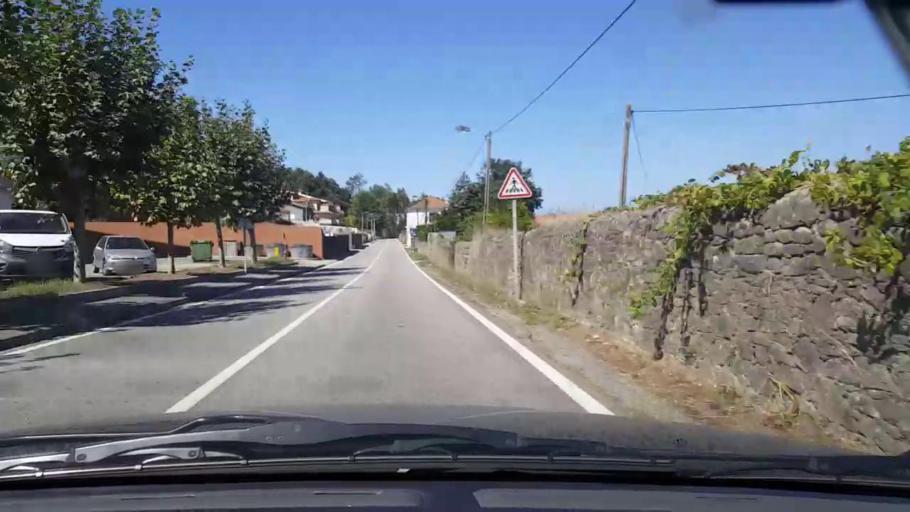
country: PT
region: Porto
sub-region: Maia
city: Gemunde
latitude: 41.3390
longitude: -8.6458
